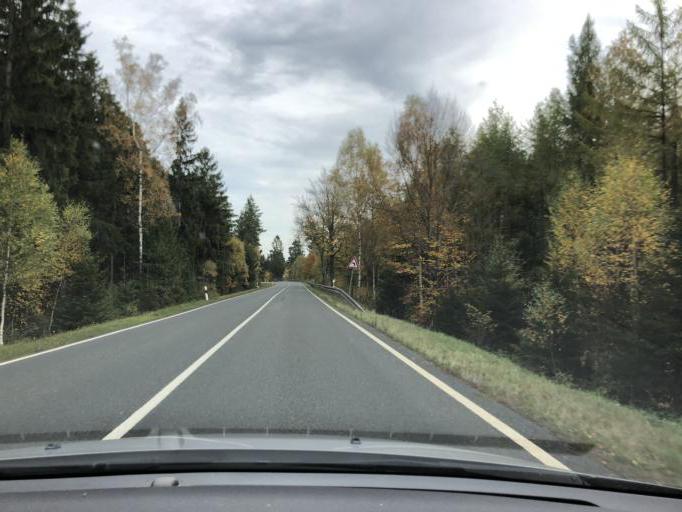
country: DE
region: Thuringia
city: Wittgendorf
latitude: 50.5791
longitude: 11.2729
